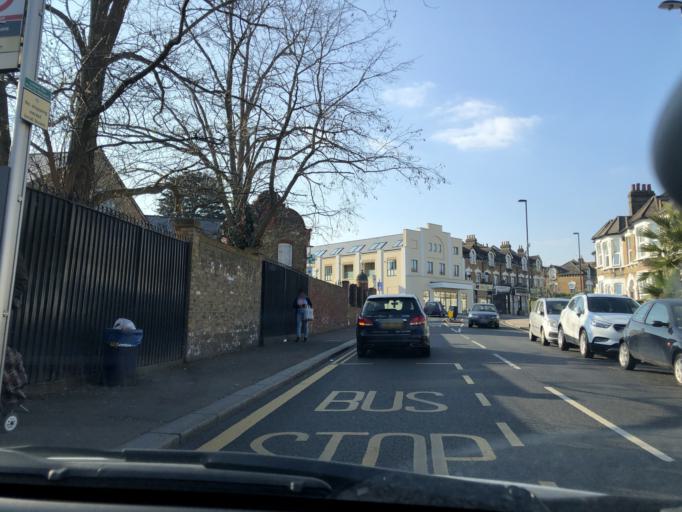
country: GB
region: England
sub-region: Greater London
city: Catford
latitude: 51.4499
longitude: -0.0047
